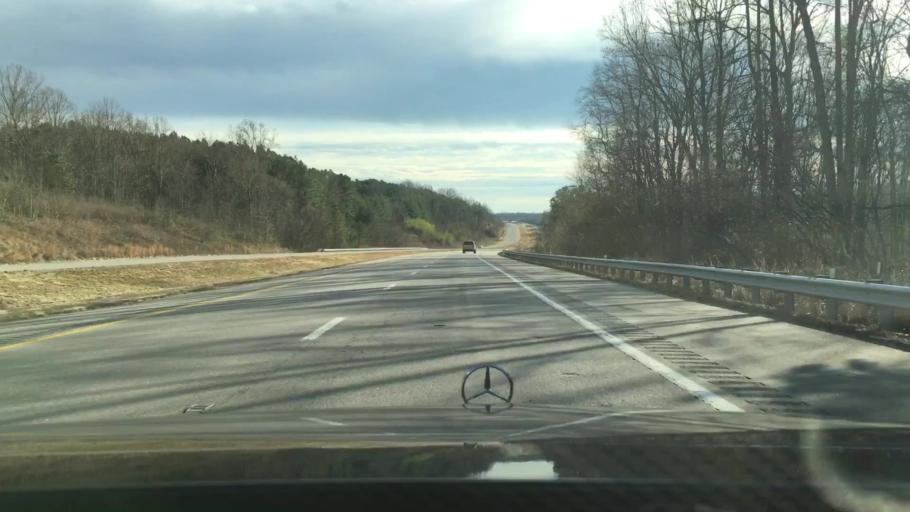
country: US
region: Virginia
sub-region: City of Danville
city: Danville
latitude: 36.6365
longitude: -79.3647
